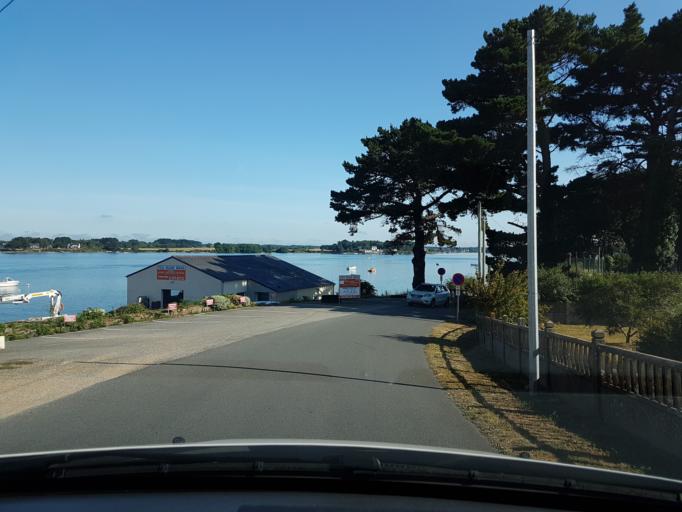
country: FR
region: Brittany
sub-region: Departement du Morbihan
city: Belz
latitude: 47.6816
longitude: -3.1899
